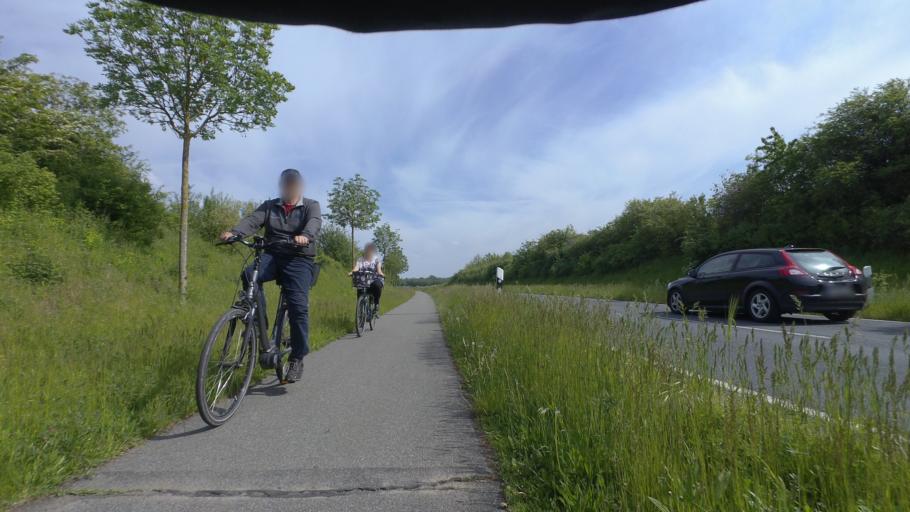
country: DE
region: Saxony-Anhalt
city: Hotensleben
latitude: 52.1241
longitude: 11.0006
